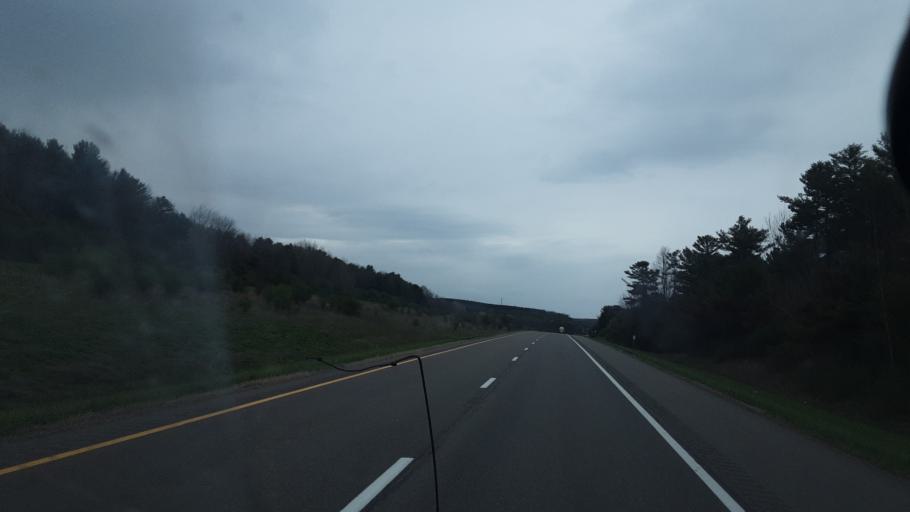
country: US
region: New York
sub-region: Allegany County
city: Alfred
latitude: 42.3022
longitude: -77.9117
